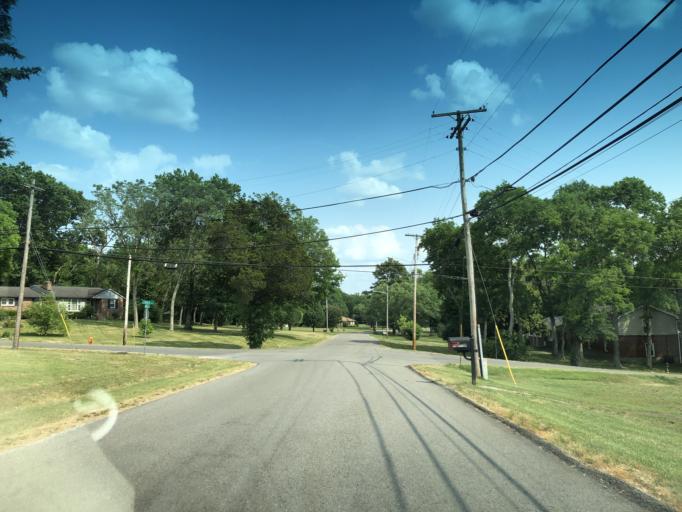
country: US
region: Tennessee
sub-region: Davidson County
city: Goodlettsville
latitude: 36.2615
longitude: -86.7247
